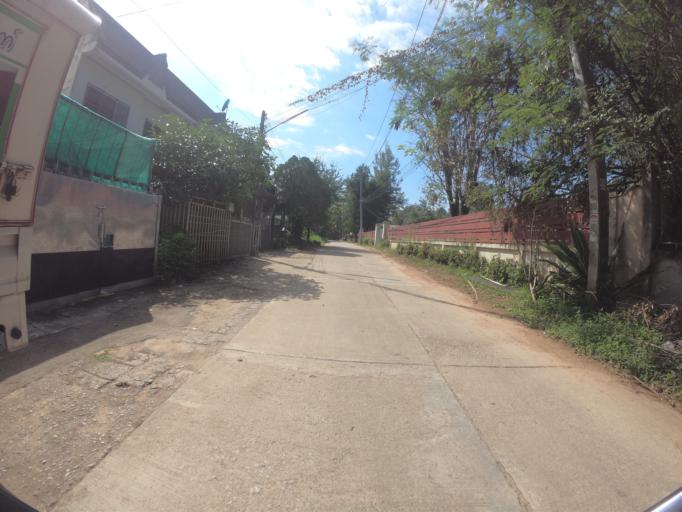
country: TH
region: Chiang Mai
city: Chiang Mai
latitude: 18.7853
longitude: 98.9572
